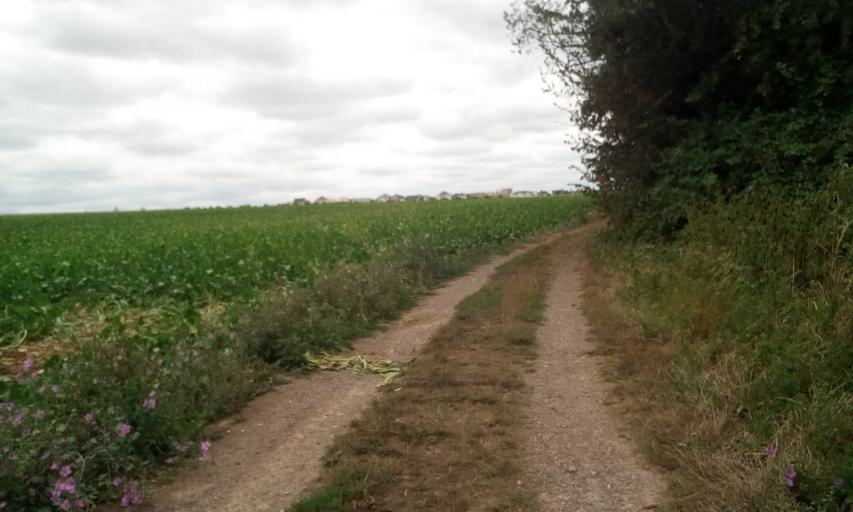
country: FR
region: Lower Normandy
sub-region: Departement du Calvados
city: Fontaine-Etoupefour
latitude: 49.1519
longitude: -0.4405
